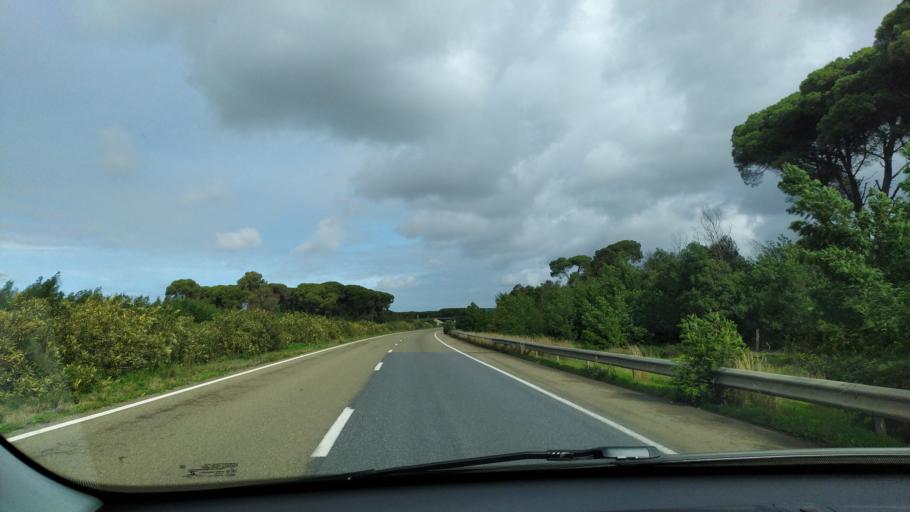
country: MA
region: Tanger-Tetouan
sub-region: Larache
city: Larache
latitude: 35.1358
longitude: -6.1470
